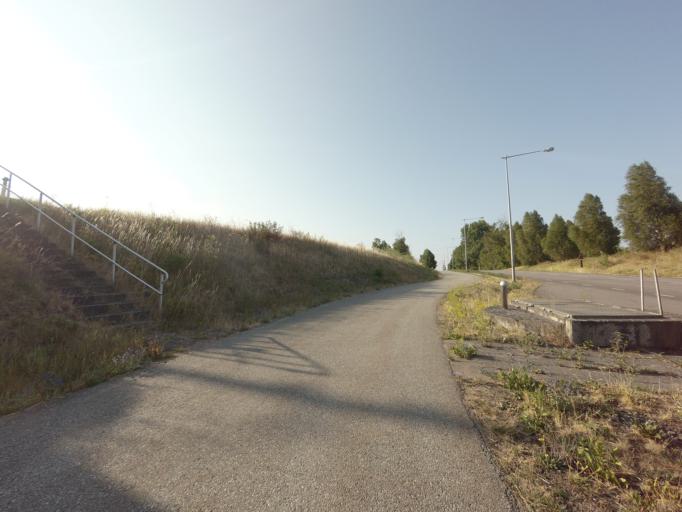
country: SE
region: Skane
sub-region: Landskrona
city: Landskrona
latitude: 55.8686
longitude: 12.8697
